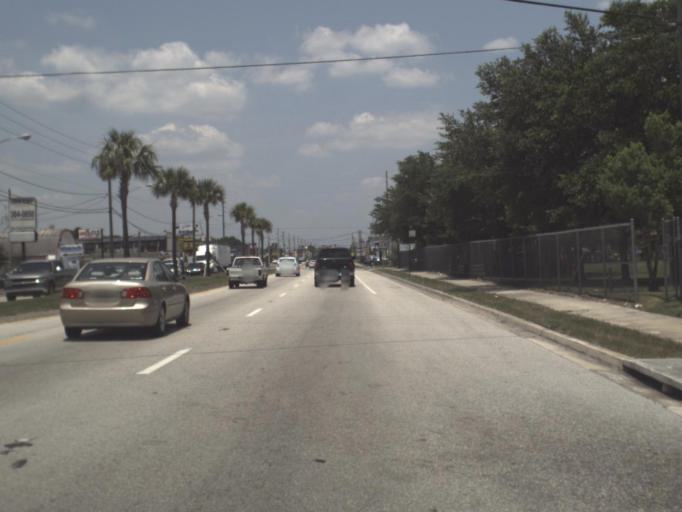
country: US
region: Florida
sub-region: Duval County
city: Jacksonville
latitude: 30.3288
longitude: -81.7308
